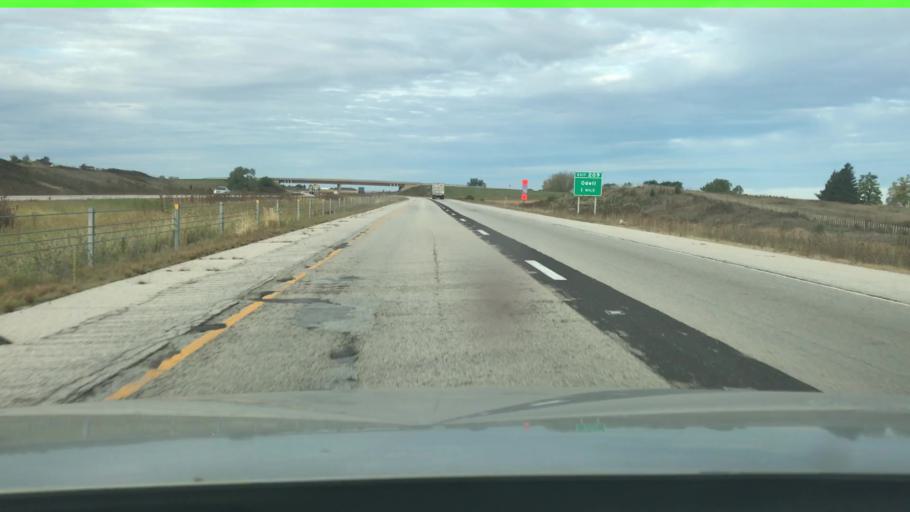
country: US
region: Illinois
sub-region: Livingston County
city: Odell
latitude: 41.0211
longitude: -88.5230
